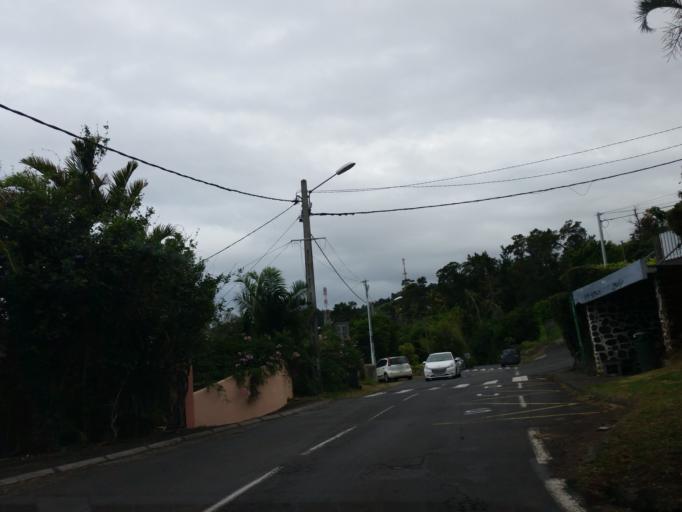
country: RE
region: Reunion
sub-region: Reunion
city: Saint-Denis
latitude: -20.8853
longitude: 55.4219
